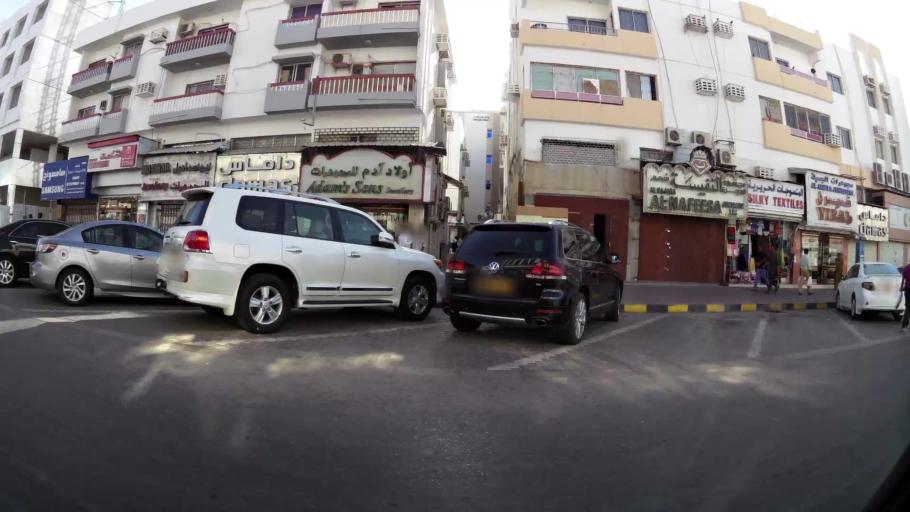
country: OM
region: Muhafazat Masqat
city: Muscat
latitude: 23.5912
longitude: 58.5448
